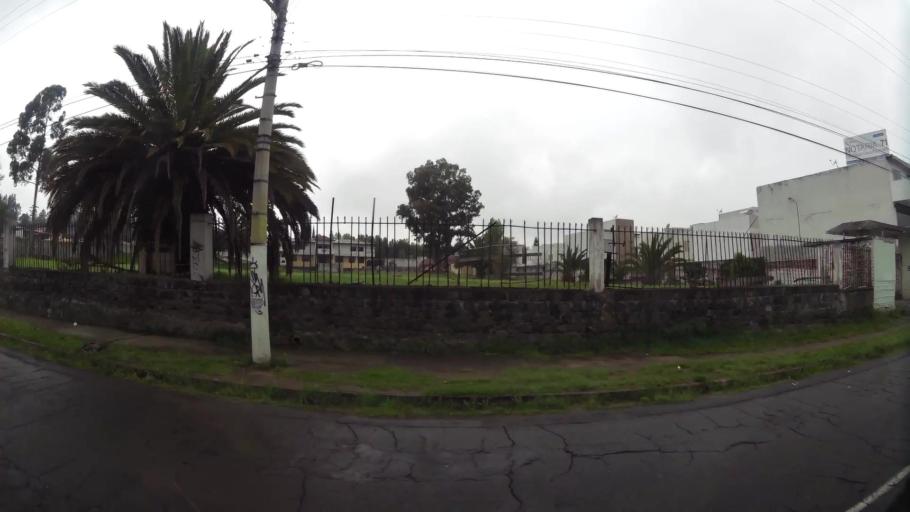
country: EC
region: Pichincha
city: Sangolqui
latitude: -0.2899
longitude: -78.4452
